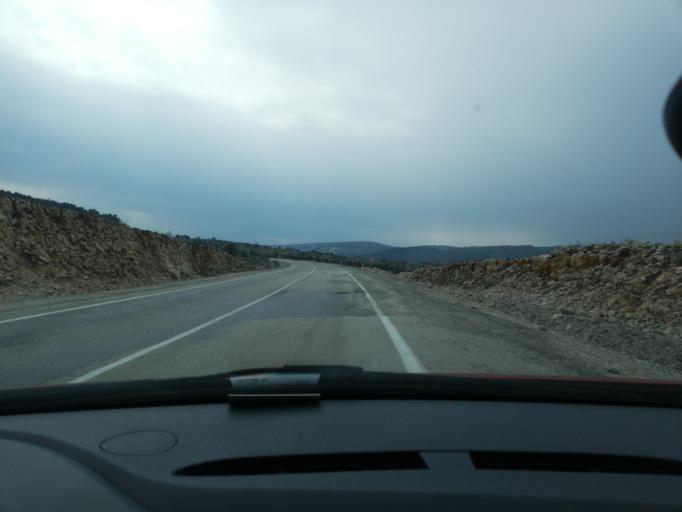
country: TR
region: Kastamonu
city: Pinarbasi
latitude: 41.5498
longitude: 33.0554
